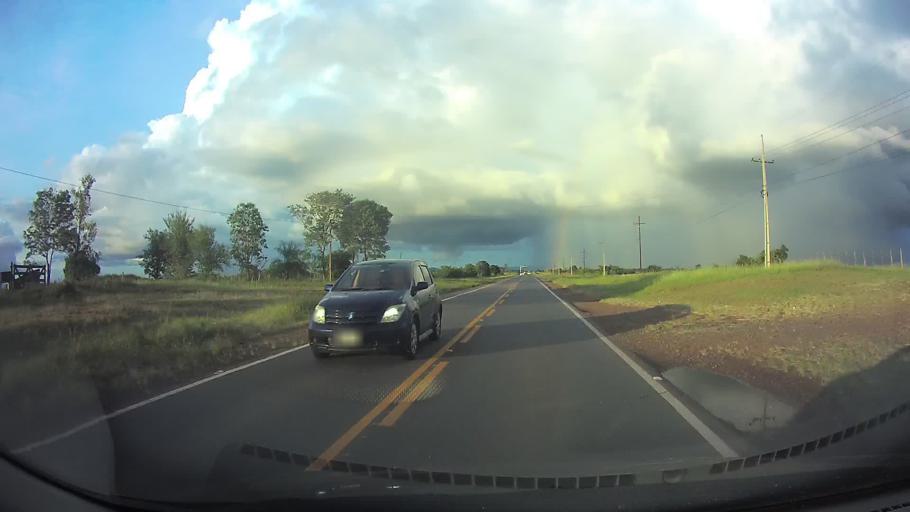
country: PY
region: Paraguari
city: Carapegua
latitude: -25.7468
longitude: -57.2148
